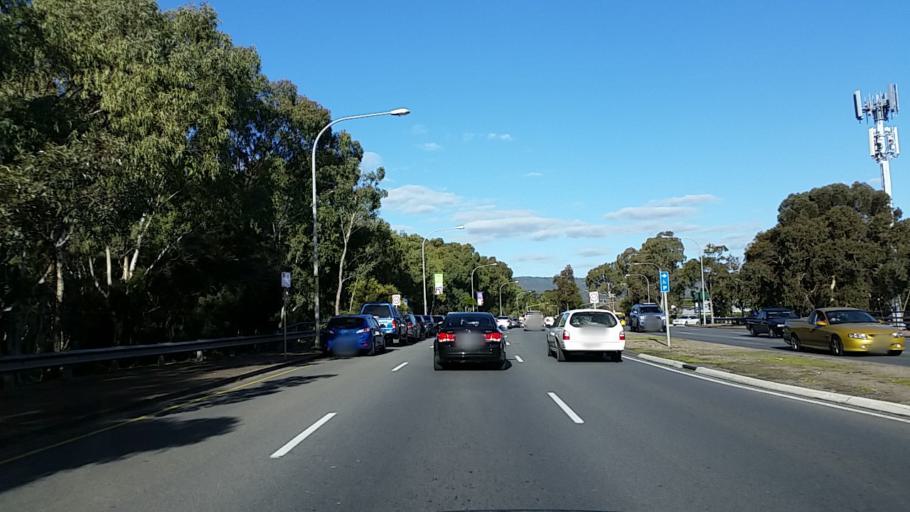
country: AU
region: South Australia
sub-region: Campbelltown
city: Paradise
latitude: -34.8671
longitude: 138.6631
